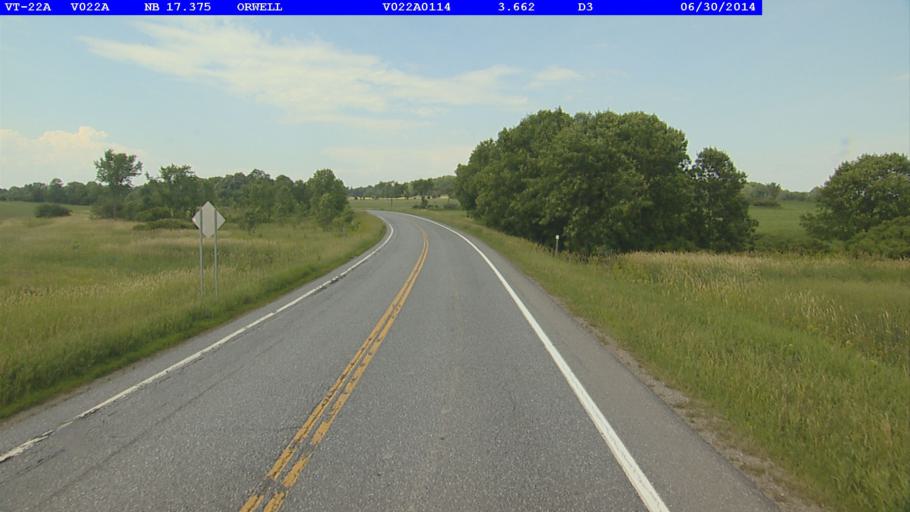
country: US
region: New York
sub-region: Essex County
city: Ticonderoga
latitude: 43.8098
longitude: -73.3040
